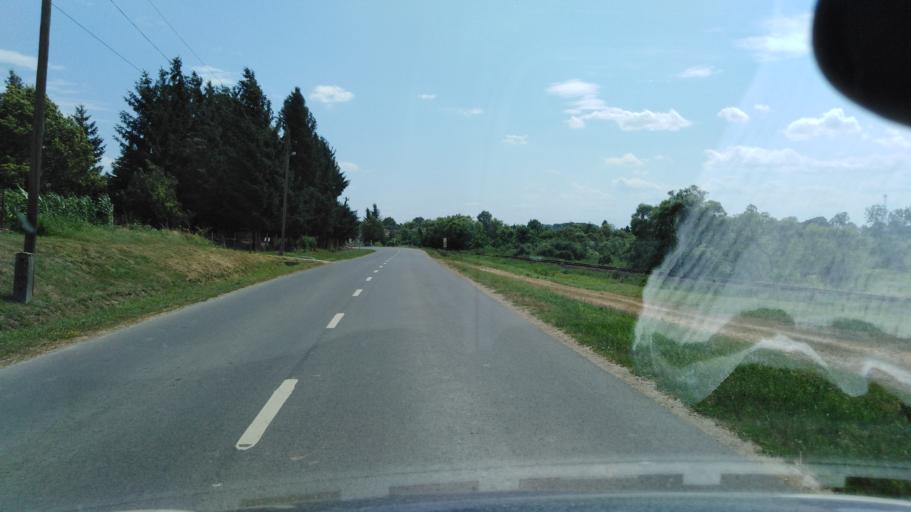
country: HU
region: Nograd
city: Szecseny
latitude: 48.1417
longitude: 19.5304
